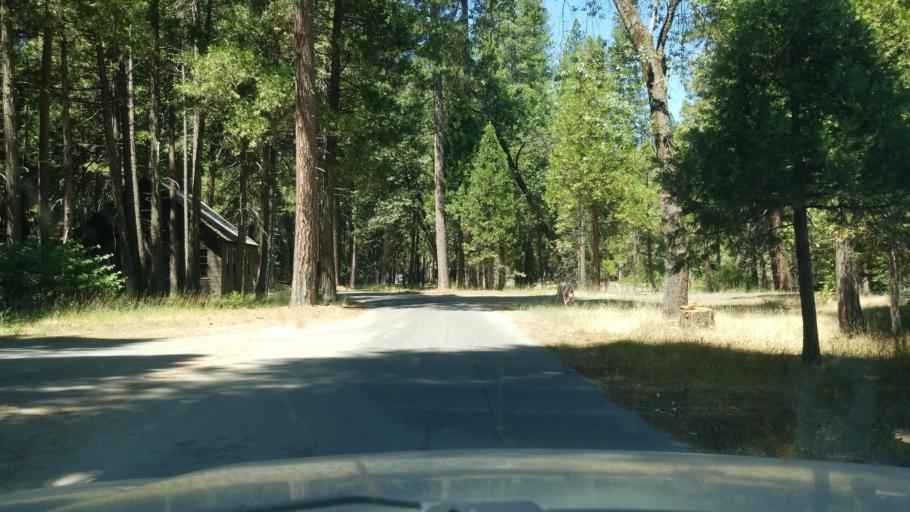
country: US
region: California
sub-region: Madera County
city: Ahwahnee
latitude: 37.5381
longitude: -119.6535
